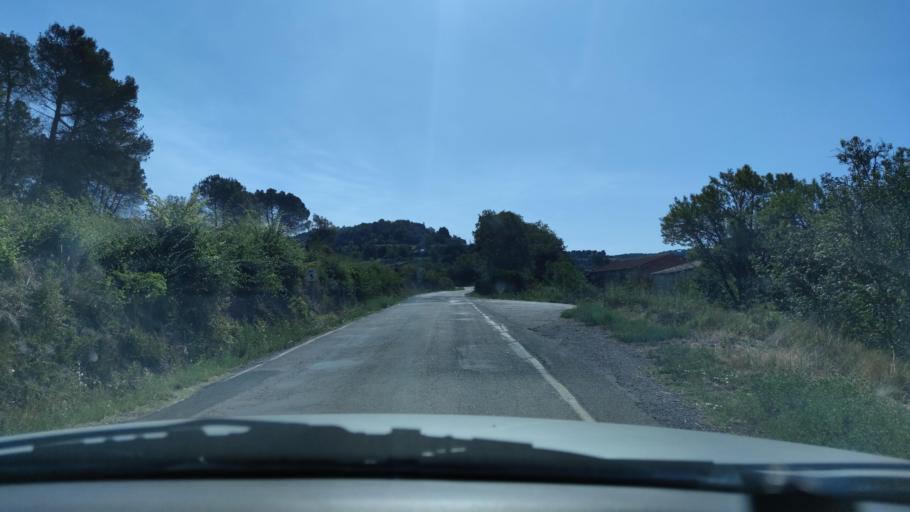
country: ES
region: Catalonia
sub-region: Provincia de Barcelona
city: Pujalt
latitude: 41.6884
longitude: 1.3850
